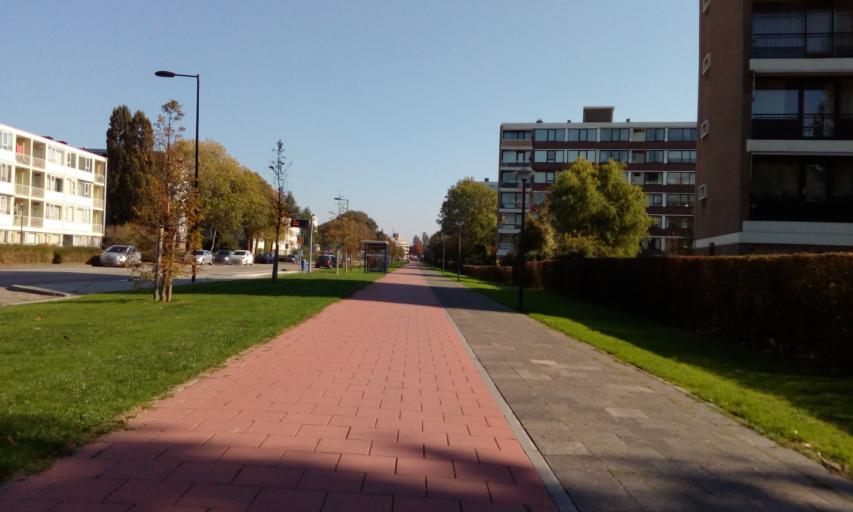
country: NL
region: South Holland
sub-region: Gemeente Vlaardingen
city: Vlaardingen
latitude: 51.9135
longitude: 4.3209
